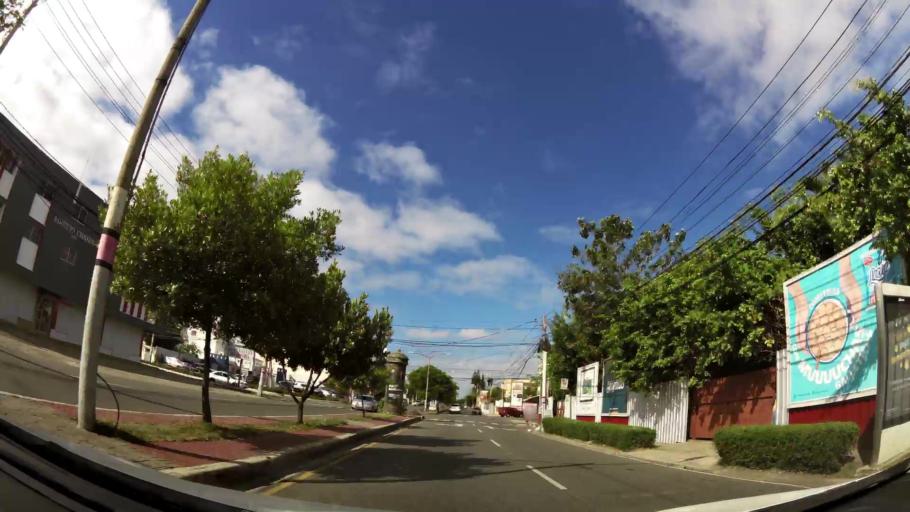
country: DO
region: Nacional
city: Bella Vista
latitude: 18.4571
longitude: -69.9403
